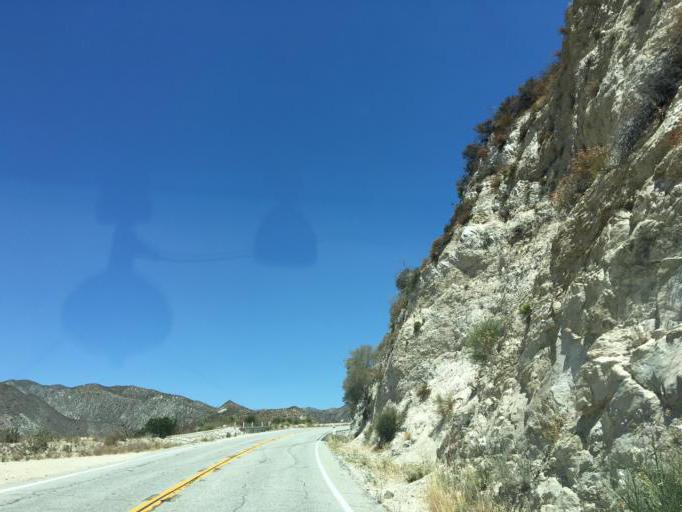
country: US
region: California
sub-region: Los Angeles County
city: La Crescenta-Montrose
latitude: 34.2952
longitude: -118.1797
